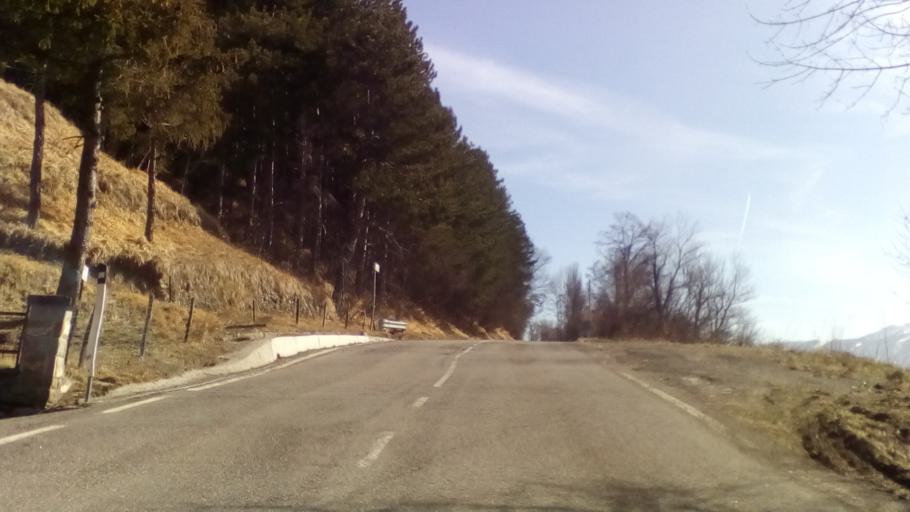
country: IT
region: Emilia-Romagna
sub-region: Provincia di Modena
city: Riolunato
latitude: 44.2573
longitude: 10.6462
